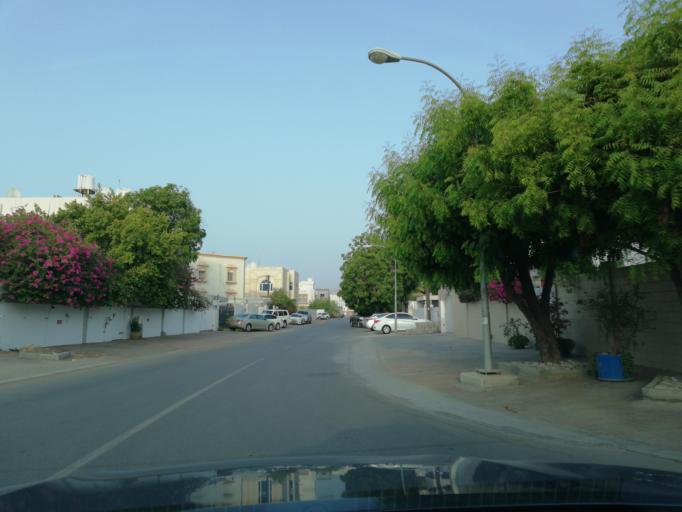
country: OM
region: Muhafazat Masqat
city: Bawshar
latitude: 23.5949
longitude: 58.3960
